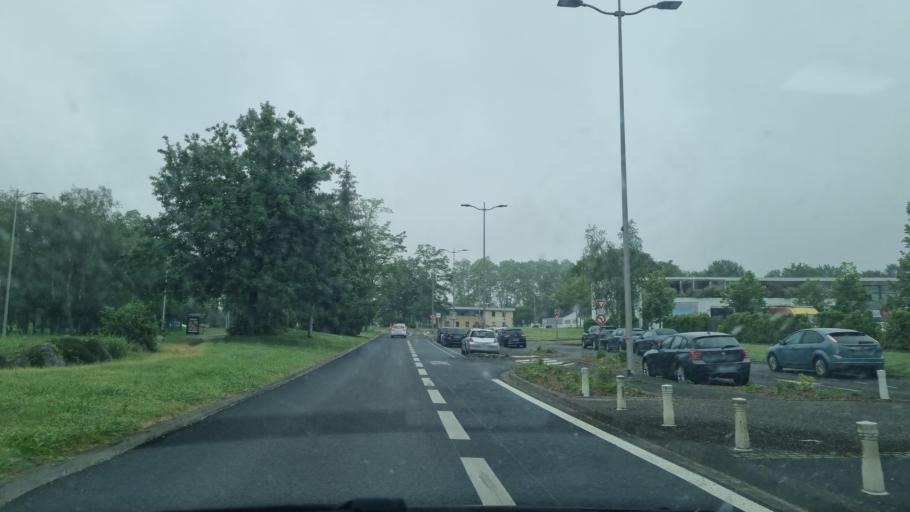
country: FR
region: Aquitaine
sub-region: Departement des Pyrenees-Atlantiques
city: Buros
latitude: 43.3222
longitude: -0.3262
